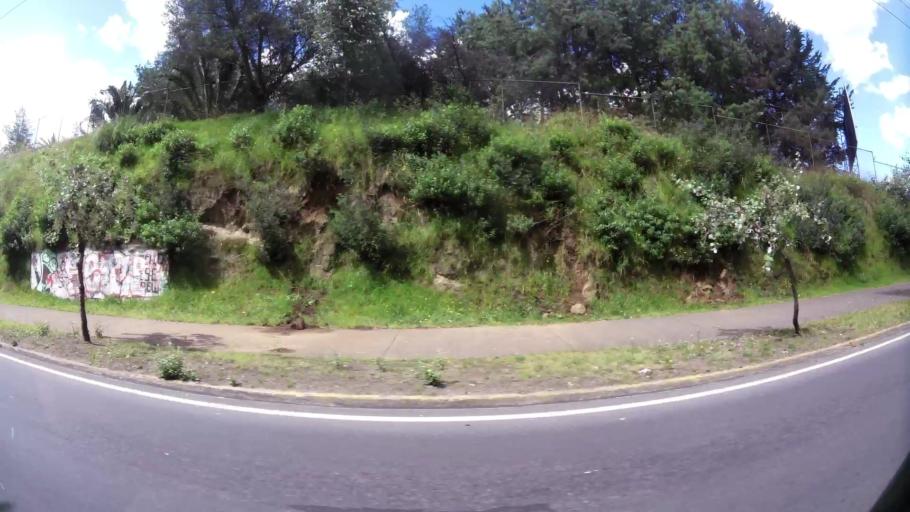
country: EC
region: Pichincha
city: Quito
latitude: -0.1583
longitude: -78.4963
